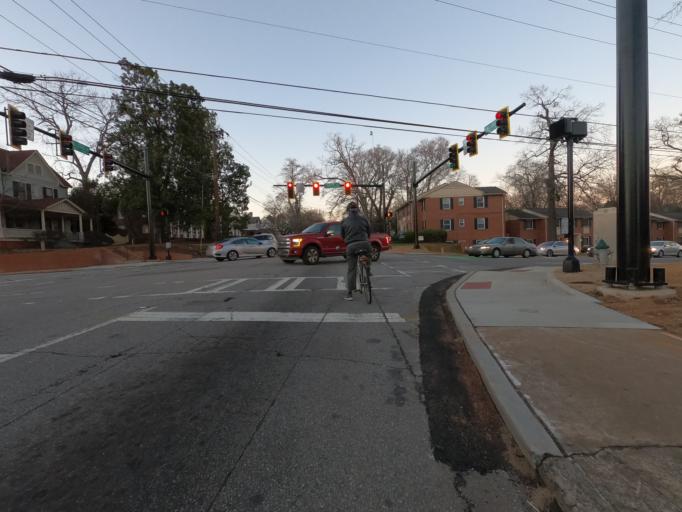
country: US
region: Georgia
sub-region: Clarke County
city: Athens
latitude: 33.9491
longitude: -83.3874
